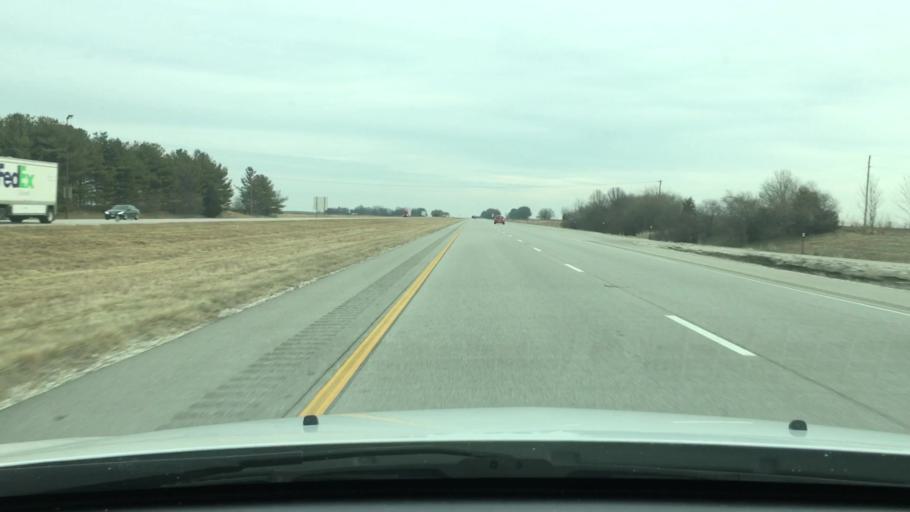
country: US
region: Illinois
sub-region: Sangamon County
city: New Berlin
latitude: 39.7368
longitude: -90.0381
